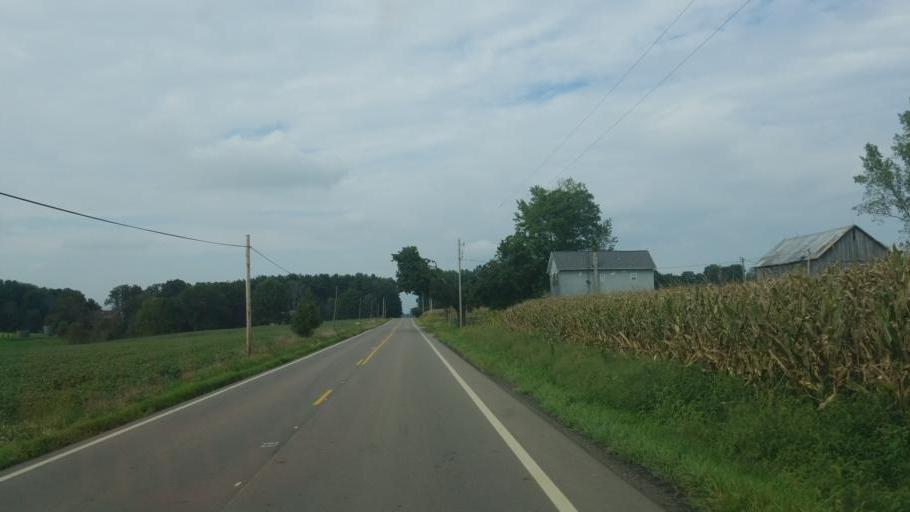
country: US
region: Ohio
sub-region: Wayne County
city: West Salem
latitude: 40.8842
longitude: -82.0531
